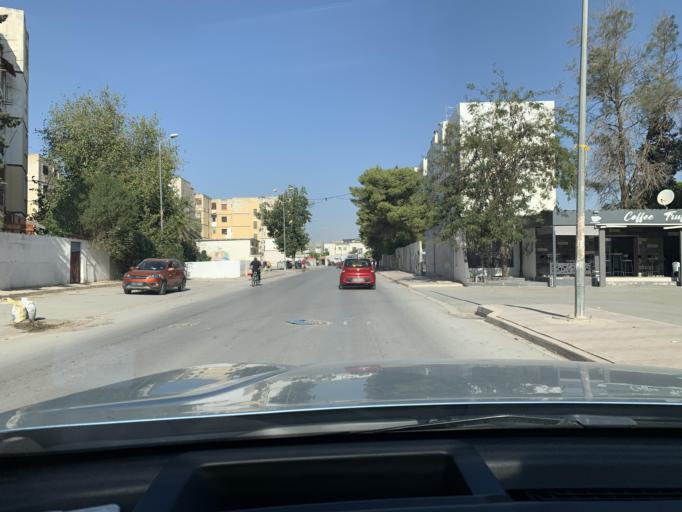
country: TN
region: Manouba
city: Manouba
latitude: 36.8245
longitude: 10.1189
